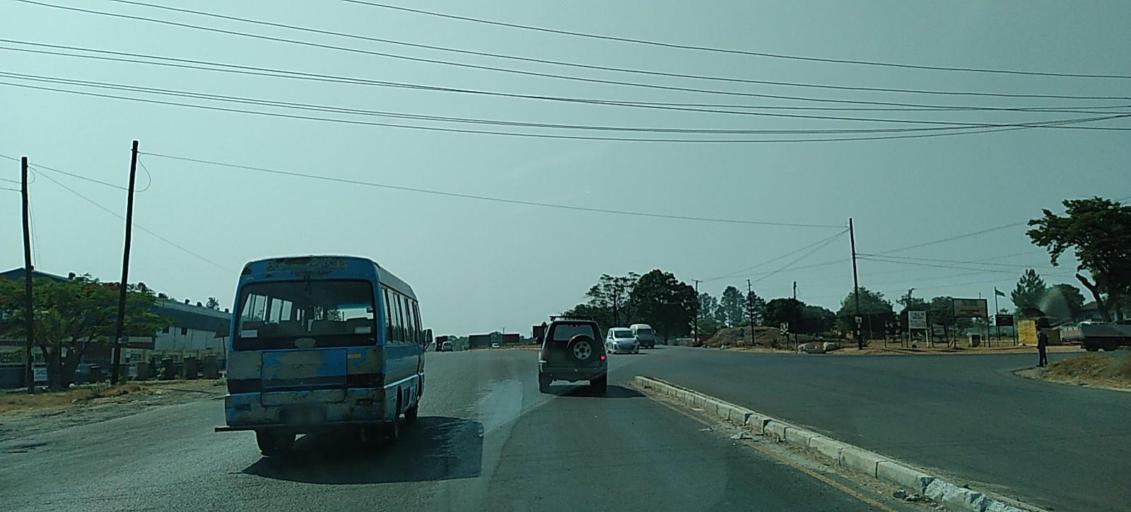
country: ZM
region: Copperbelt
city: Chingola
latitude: -12.5564
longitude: 27.8732
